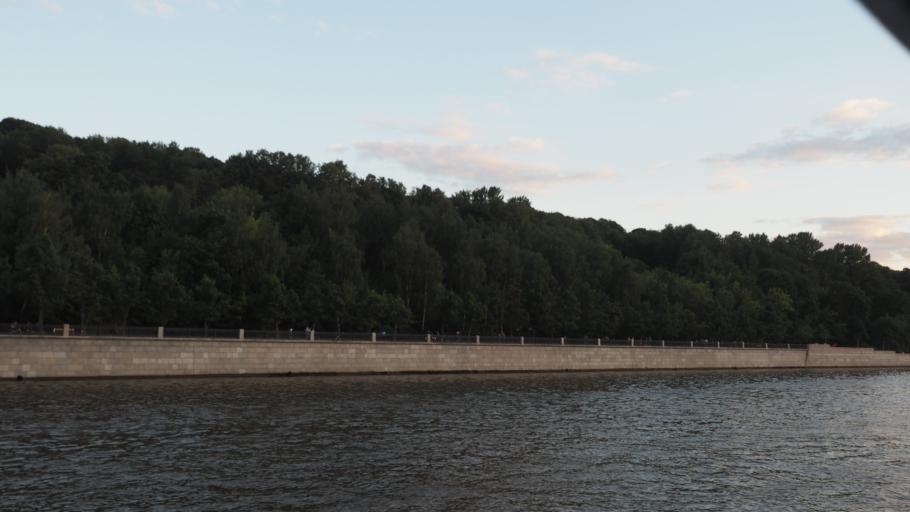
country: RU
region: Moskovskaya
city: Leninskiye Gory
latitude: 55.7122
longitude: 37.5715
